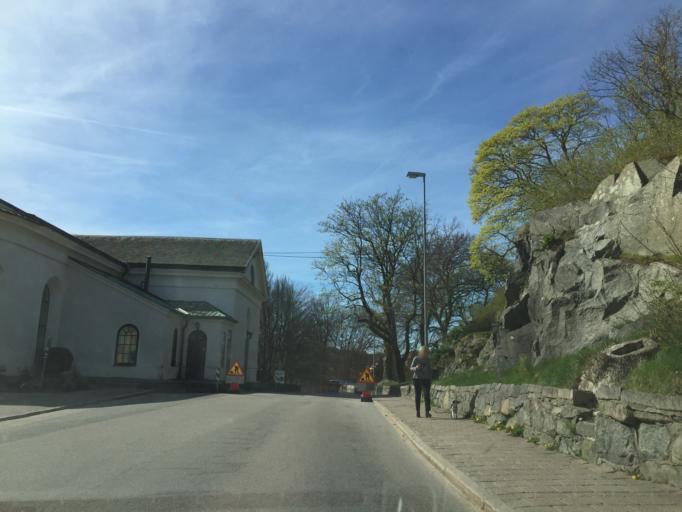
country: SE
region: Vaestra Goetaland
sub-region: Uddevalla Kommun
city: Uddevalla
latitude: 58.3479
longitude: 11.9410
